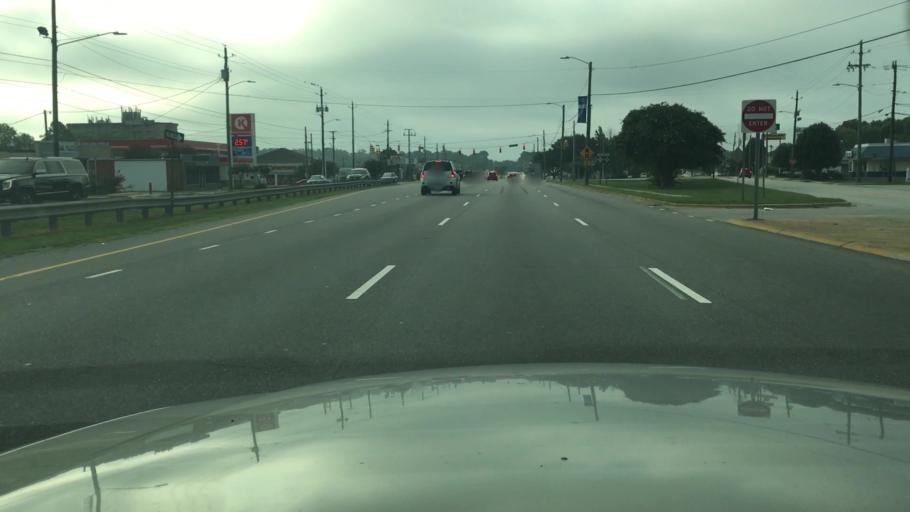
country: US
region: North Carolina
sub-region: Cumberland County
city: Fayetteville
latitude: 35.0756
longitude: -78.9321
